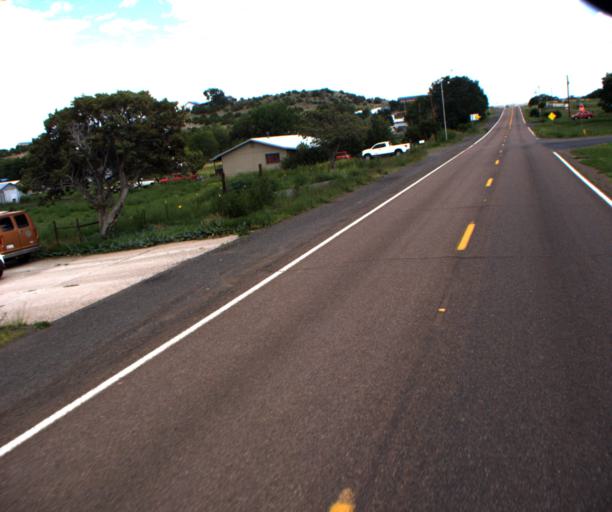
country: US
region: Arizona
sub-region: Apache County
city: Eagar
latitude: 34.1109
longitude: -109.2867
